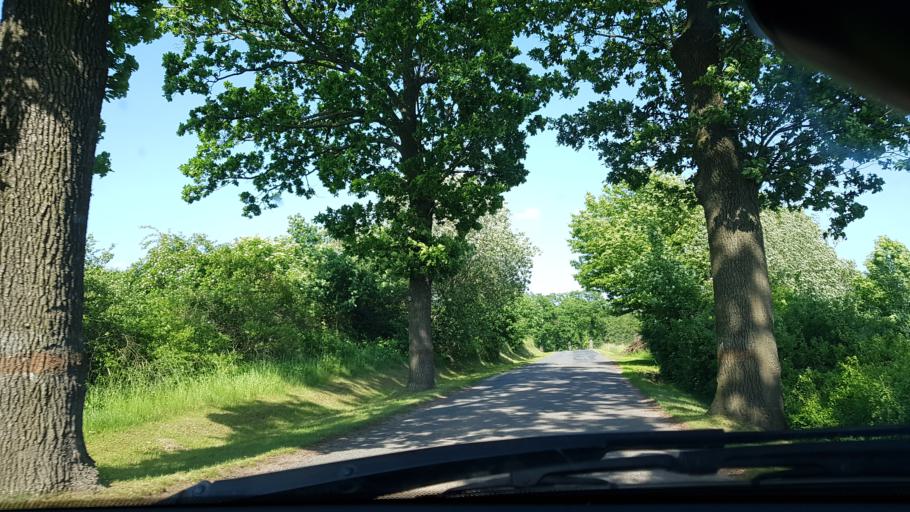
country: PL
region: Lower Silesian Voivodeship
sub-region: Powiat klodzki
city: Bozkow
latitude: 50.5187
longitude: 16.6512
